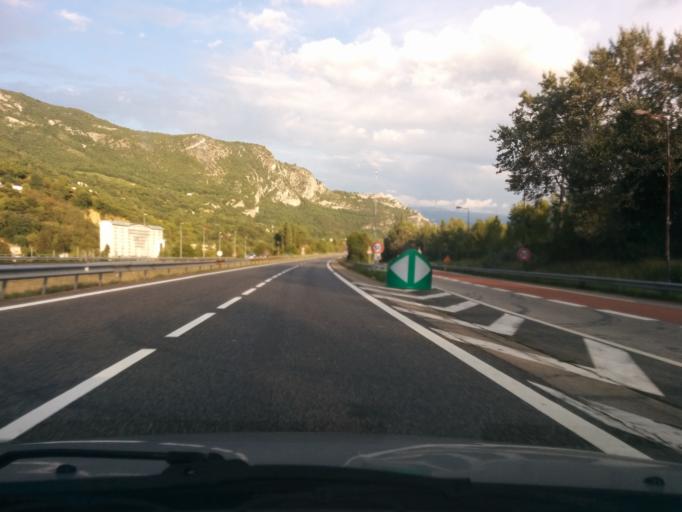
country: FR
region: Rhone-Alpes
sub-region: Departement de l'Isere
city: Fontaine
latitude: 45.2099
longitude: 5.6981
